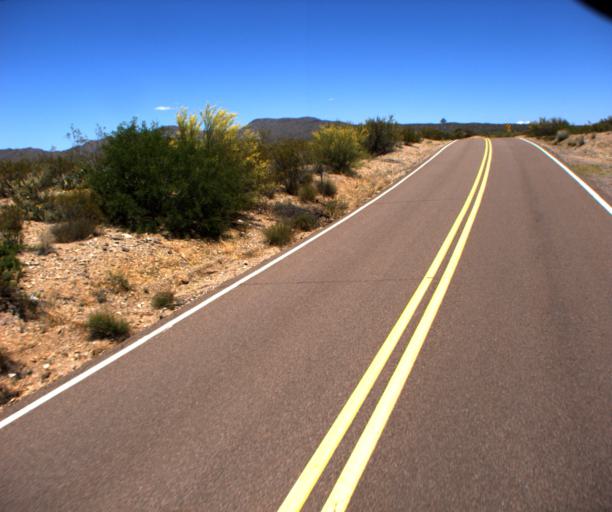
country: US
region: Arizona
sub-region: Yavapai County
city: Bagdad
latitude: 34.4666
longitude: -113.2227
